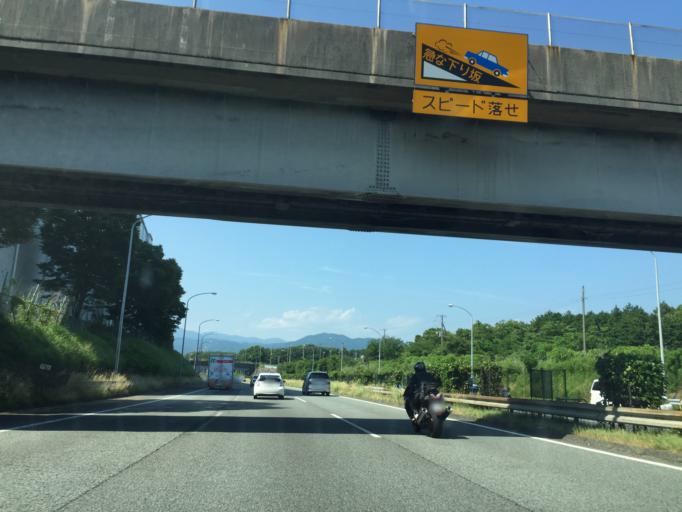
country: JP
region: Shizuoka
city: Gotemba
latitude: 35.3222
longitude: 138.9720
